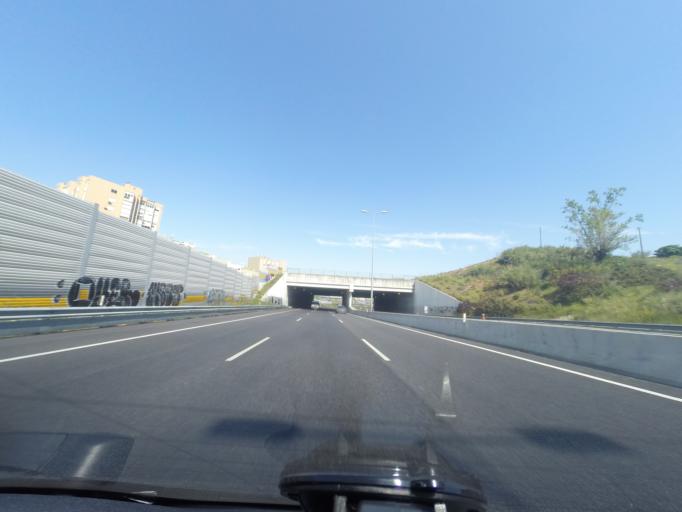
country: PT
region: Lisbon
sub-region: Odivelas
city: Pontinha
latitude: 38.7647
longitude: -9.2040
